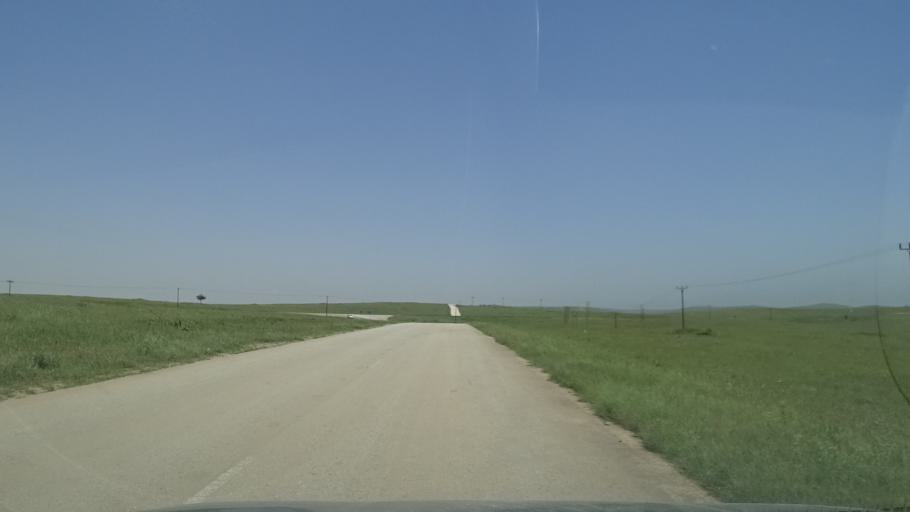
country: OM
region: Zufar
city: Salalah
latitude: 17.2498
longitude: 54.2733
